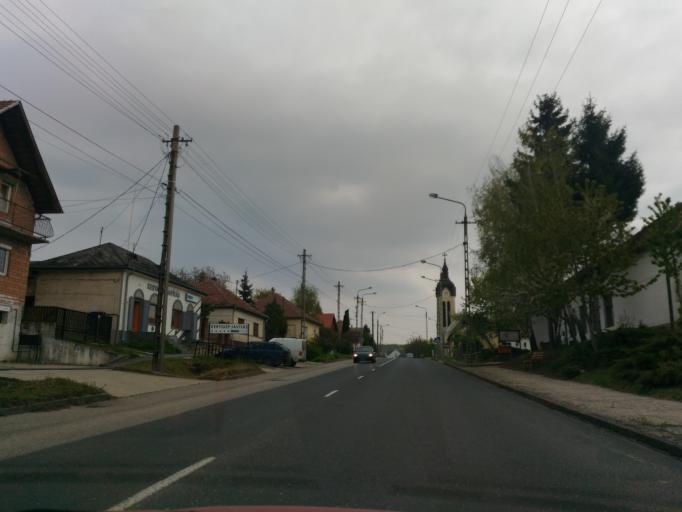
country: HU
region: Pest
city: Kerepes
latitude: 47.5628
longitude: 19.2883
